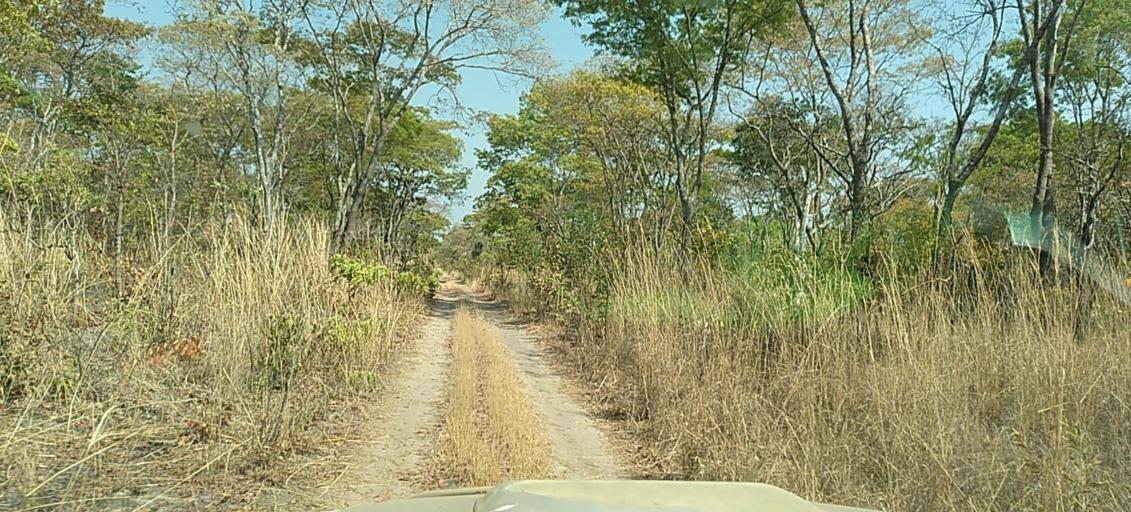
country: ZM
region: North-Western
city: Kalengwa
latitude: -13.3316
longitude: 24.8438
